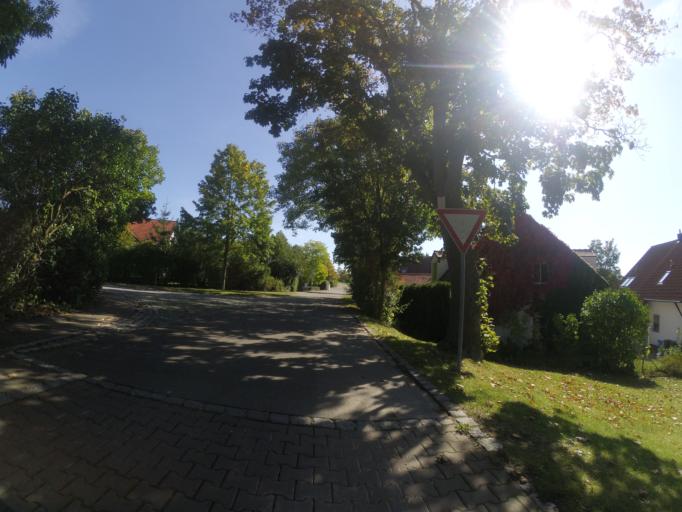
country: DE
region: Baden-Wuerttemberg
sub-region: Tuebingen Region
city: Langenau
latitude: 48.4993
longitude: 10.1098
